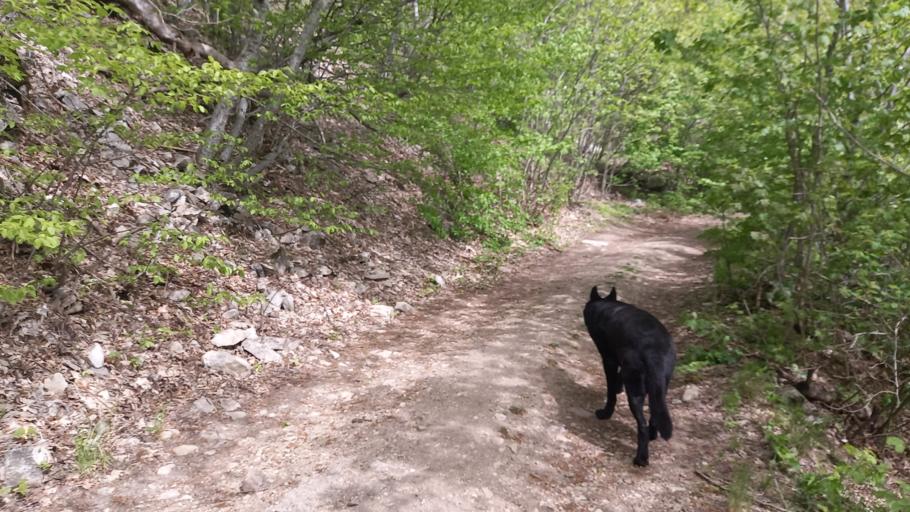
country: RU
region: Stavropol'skiy
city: Zheleznovodsk
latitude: 44.0905
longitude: 43.0297
